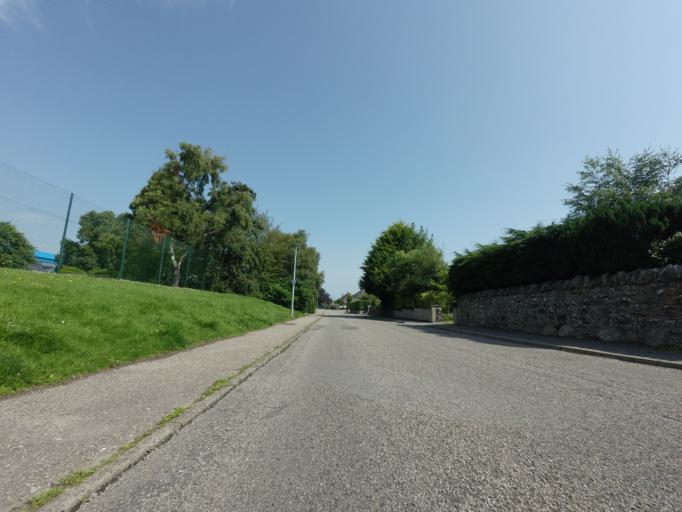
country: GB
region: Scotland
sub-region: Highland
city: Tain
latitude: 57.8066
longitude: -4.0567
